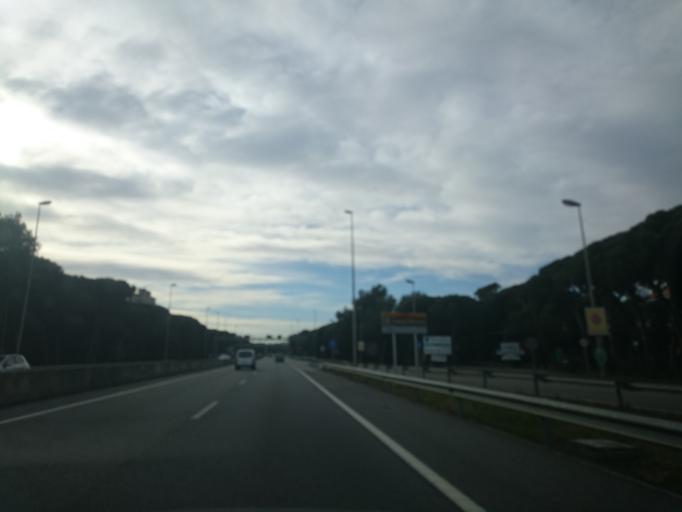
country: ES
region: Catalonia
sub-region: Provincia de Barcelona
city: Gava
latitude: 41.2699
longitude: 2.0142
